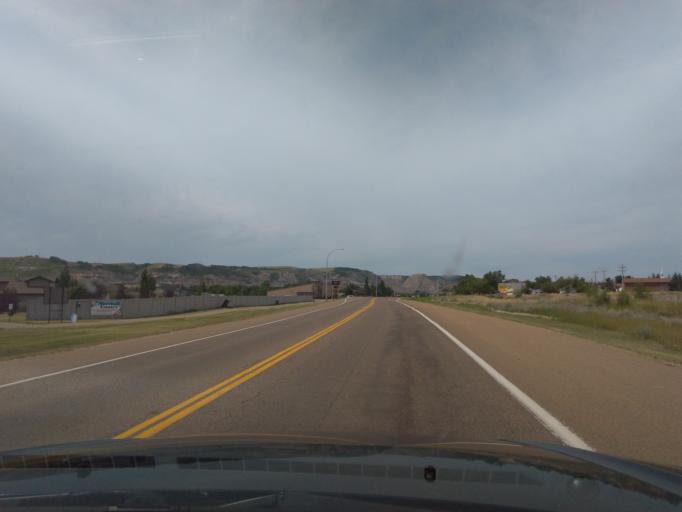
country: CA
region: Alberta
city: Three Hills
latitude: 51.4701
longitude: -112.7393
